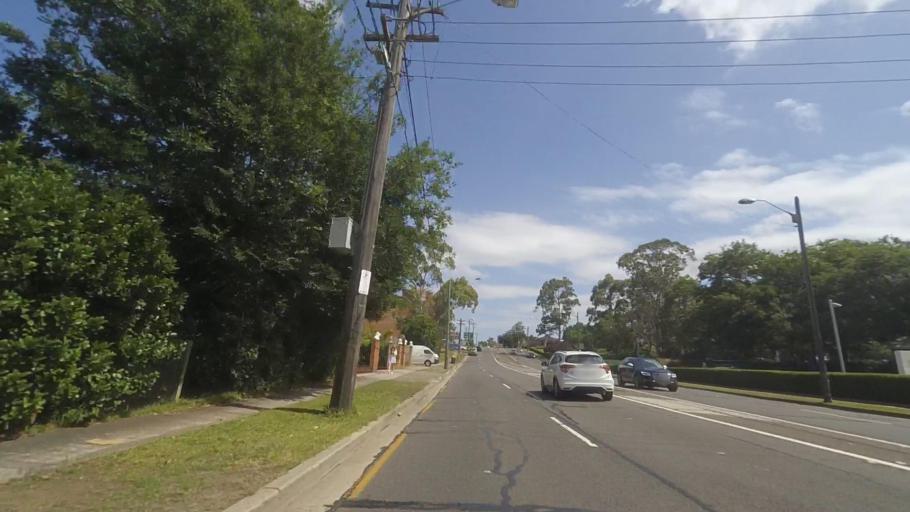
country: AU
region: New South Wales
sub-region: Parramatta
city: Carlingford
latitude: -33.7743
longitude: 151.0513
